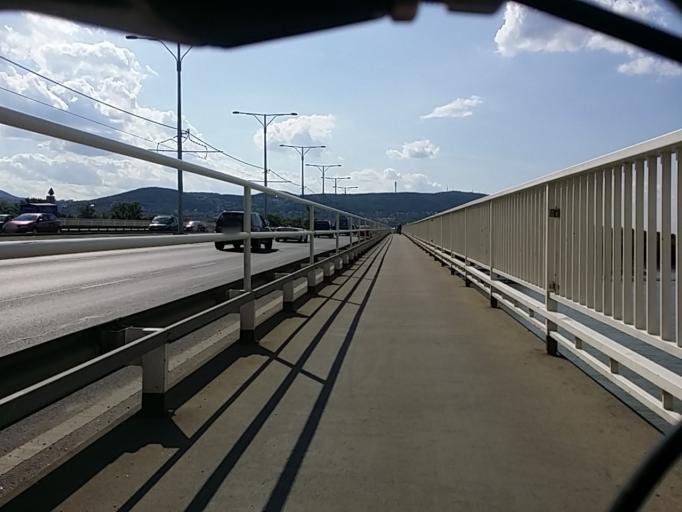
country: HU
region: Budapest
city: Budapest III. keruelet
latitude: 47.5367
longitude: 19.0581
